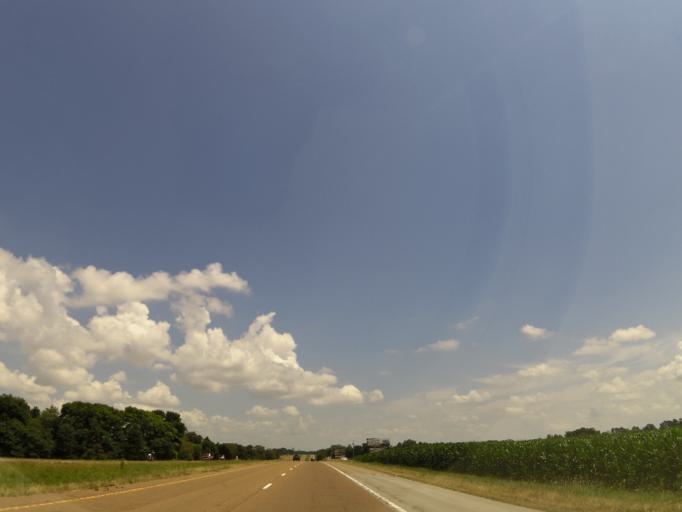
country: US
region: Tennessee
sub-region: Lauderdale County
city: Halls
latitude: 35.9489
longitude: -89.3102
